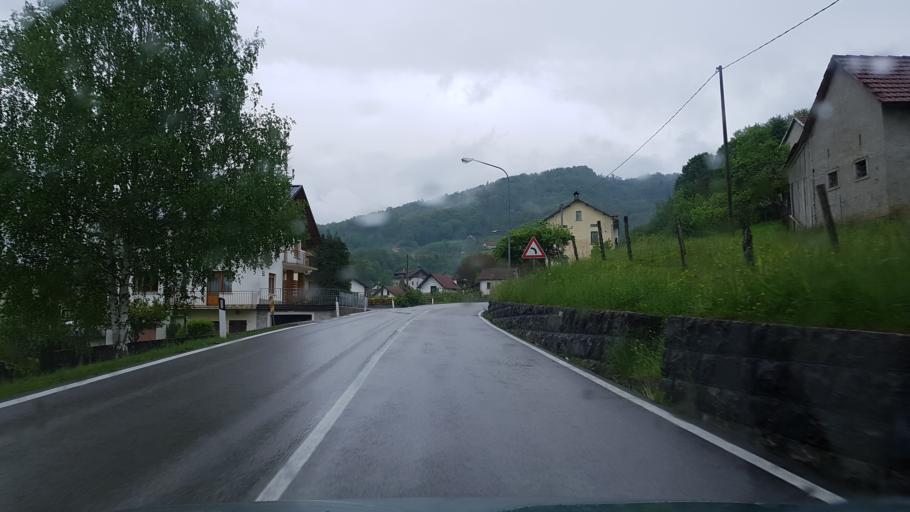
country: IT
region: Veneto
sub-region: Provincia di Belluno
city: Puos d'Alpago
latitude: 46.1384
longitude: 12.3770
